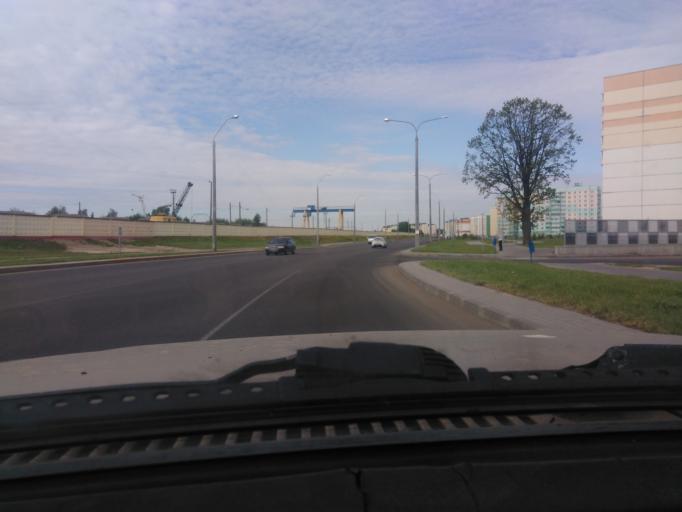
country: BY
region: Mogilev
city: Mahilyow
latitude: 53.9176
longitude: 30.3014
